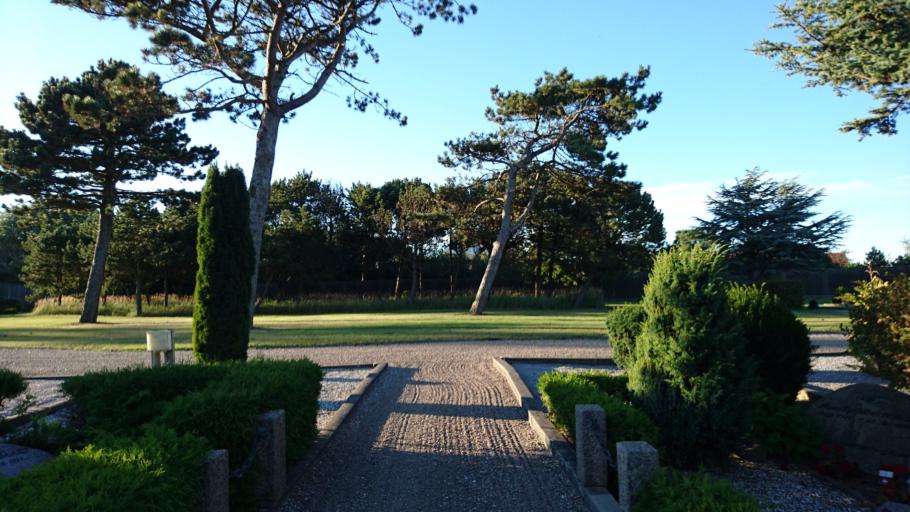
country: DK
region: North Denmark
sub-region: Frederikshavn Kommune
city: Skagen
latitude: 57.7243
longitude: 10.5842
